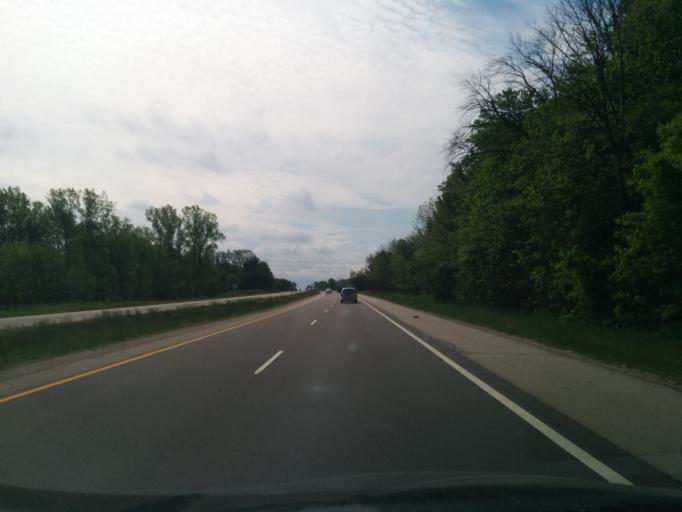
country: US
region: Michigan
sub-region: Ottawa County
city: Beechwood
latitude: 42.9149
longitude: -86.1440
